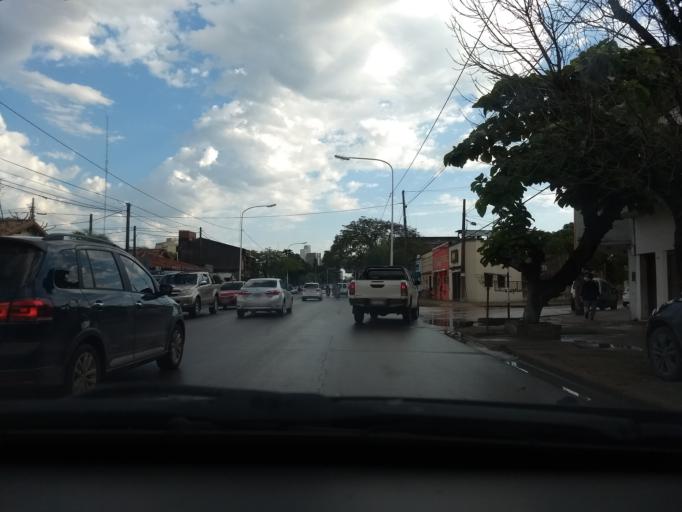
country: AR
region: Corrientes
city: Corrientes
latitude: -27.4791
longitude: -58.8288
